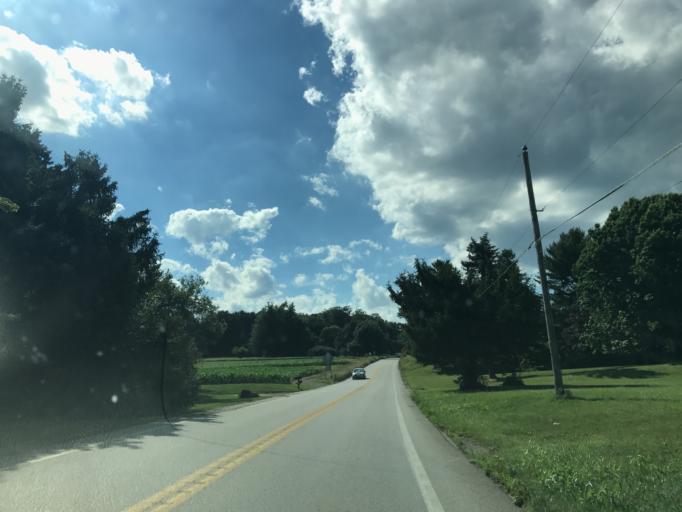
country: US
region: Pennsylvania
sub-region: York County
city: Glen Rock
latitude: 39.7429
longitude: -76.7990
